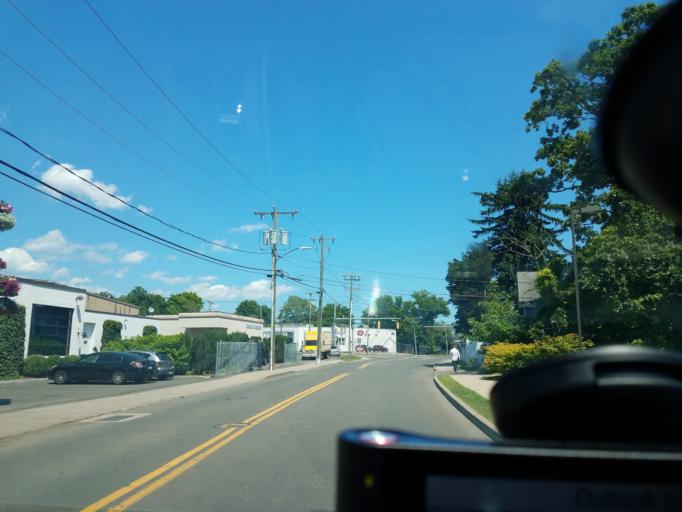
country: US
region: Connecticut
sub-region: Fairfield County
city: Old Greenwich
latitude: 41.0413
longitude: -73.5603
